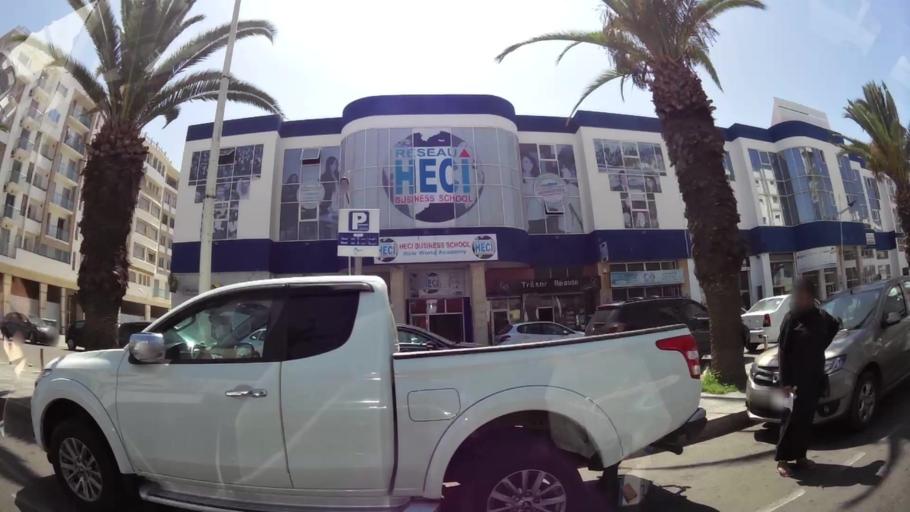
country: MA
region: Souss-Massa-Draa
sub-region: Agadir-Ida-ou-Tnan
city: Agadir
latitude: 30.4147
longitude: -9.5939
